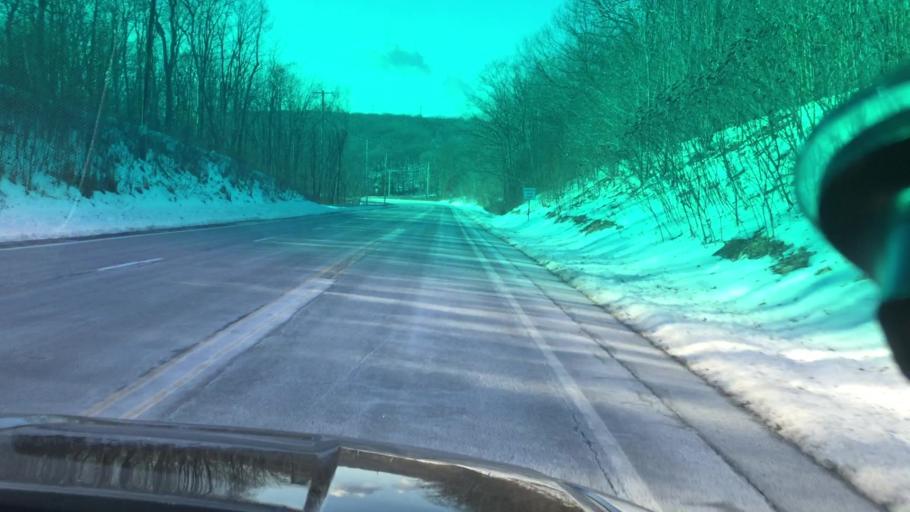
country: US
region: Pennsylvania
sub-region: Luzerne County
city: Oakdale
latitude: 41.0184
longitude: -75.9293
